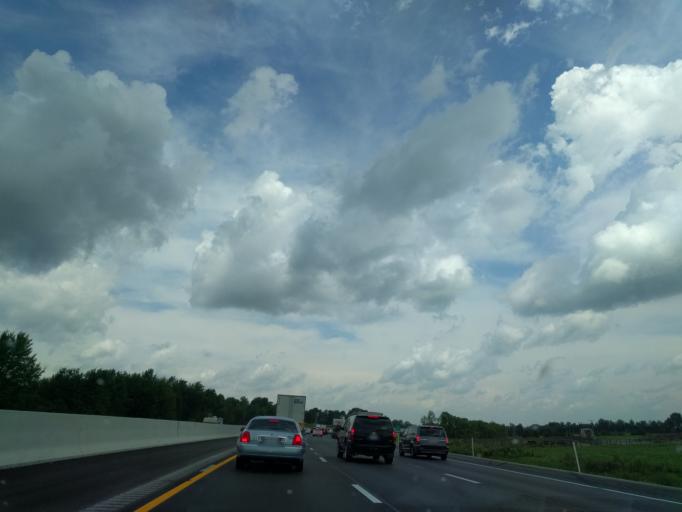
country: US
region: Kentucky
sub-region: Larue County
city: Hodgenville
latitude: 37.4992
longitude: -85.8858
